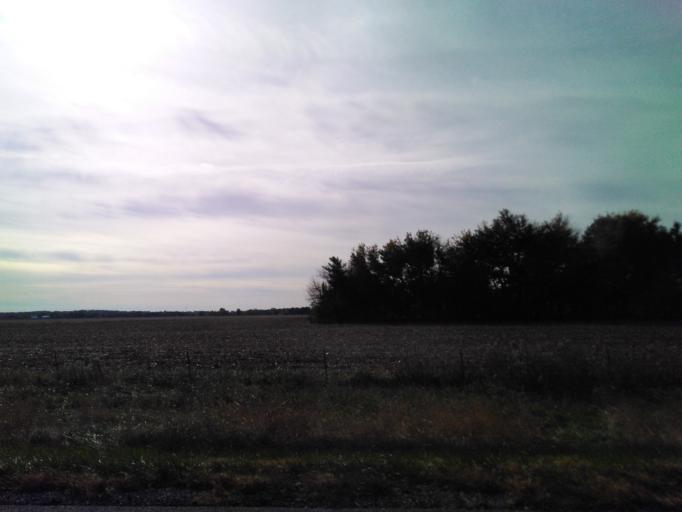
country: US
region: Illinois
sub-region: Madison County
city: Highland
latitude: 38.7850
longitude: -89.7196
